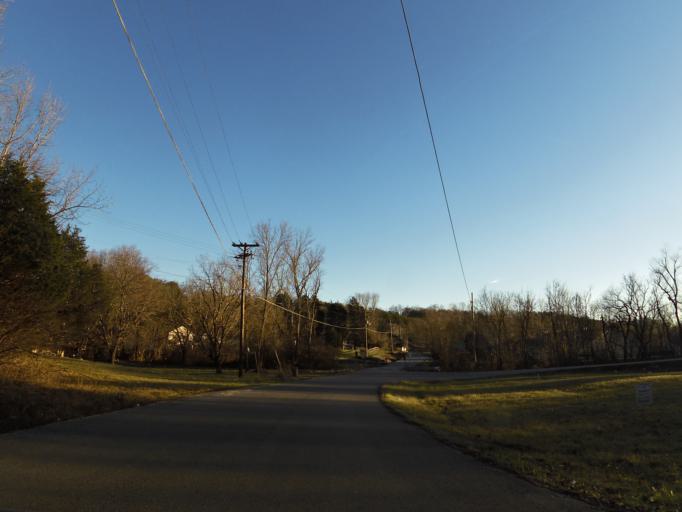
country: US
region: Tennessee
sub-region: Knox County
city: Knoxville
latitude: 35.9201
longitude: -83.8247
